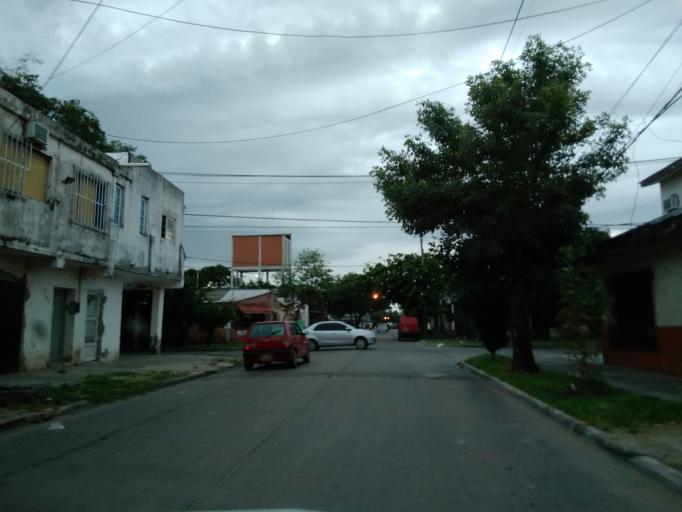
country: AR
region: Corrientes
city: Corrientes
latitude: -27.4785
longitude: -58.8237
